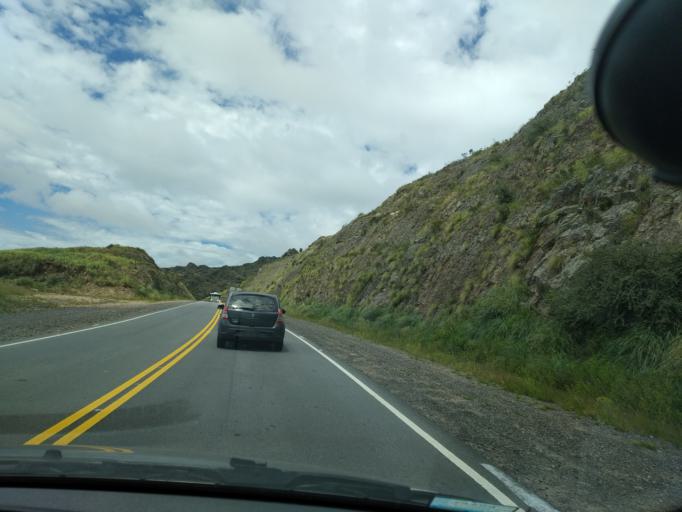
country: AR
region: Cordoba
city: Cuesta Blanca
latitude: -31.6053
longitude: -64.6961
